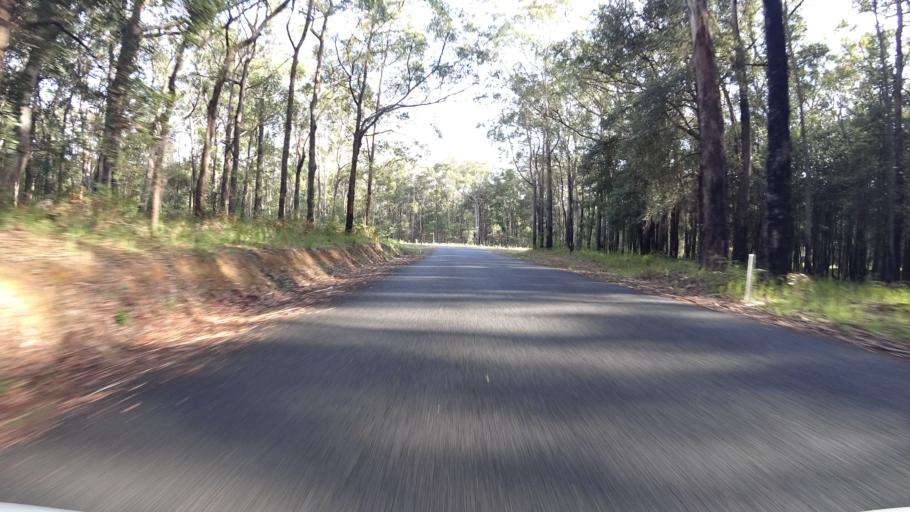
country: AU
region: New South Wales
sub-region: Shoalhaven Shire
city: Milton
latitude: -35.2546
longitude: 150.5060
